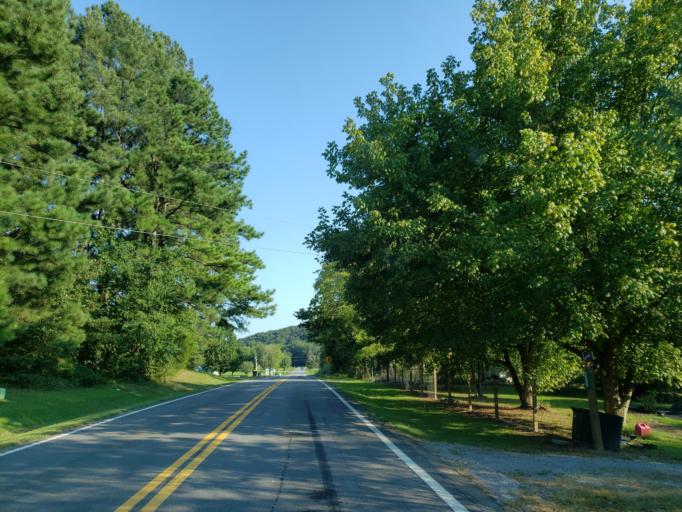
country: US
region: Tennessee
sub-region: Bradley County
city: Wildwood Lake
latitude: 35.0092
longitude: -84.7881
